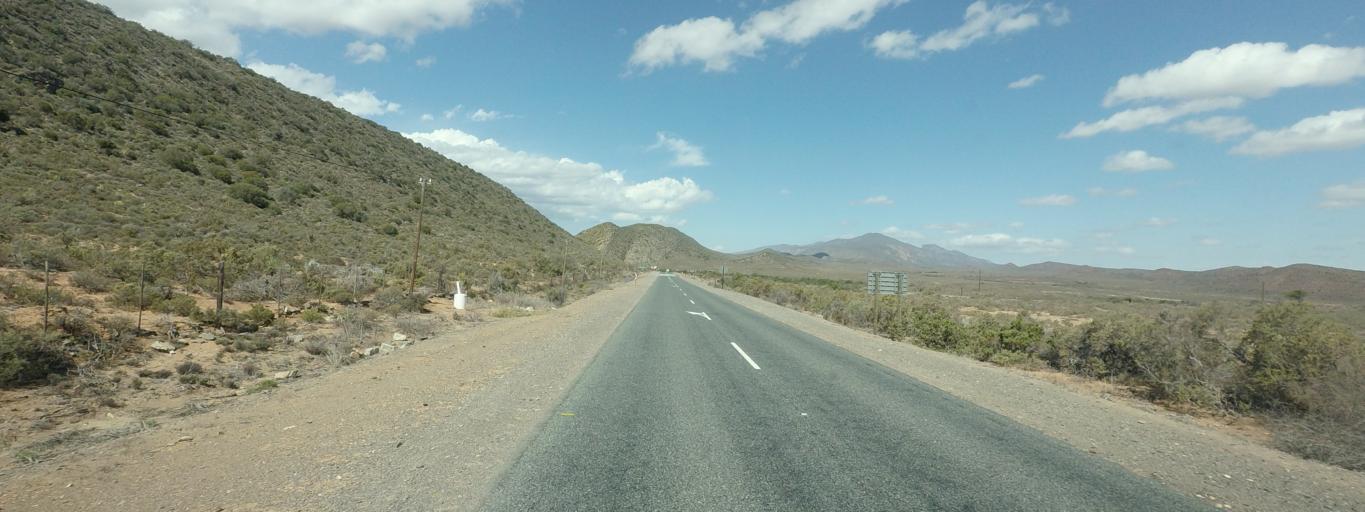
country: ZA
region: Western Cape
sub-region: Eden District Municipality
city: Ladismith
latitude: -33.5890
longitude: 21.1806
